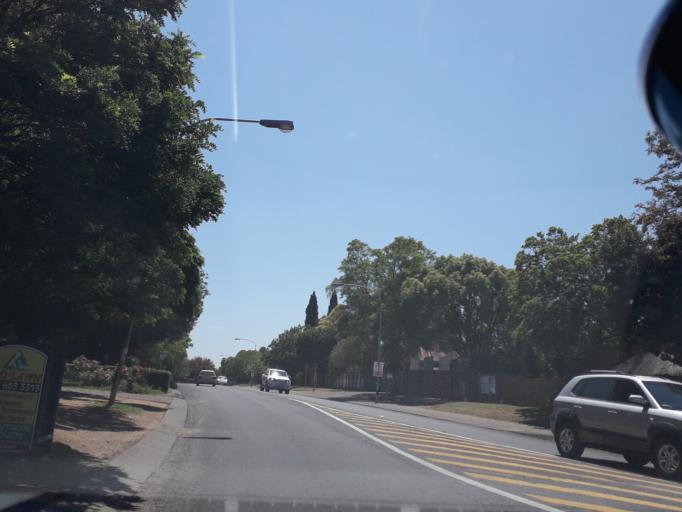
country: ZA
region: Gauteng
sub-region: City of Tshwane Metropolitan Municipality
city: Centurion
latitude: -25.8931
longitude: 28.1462
